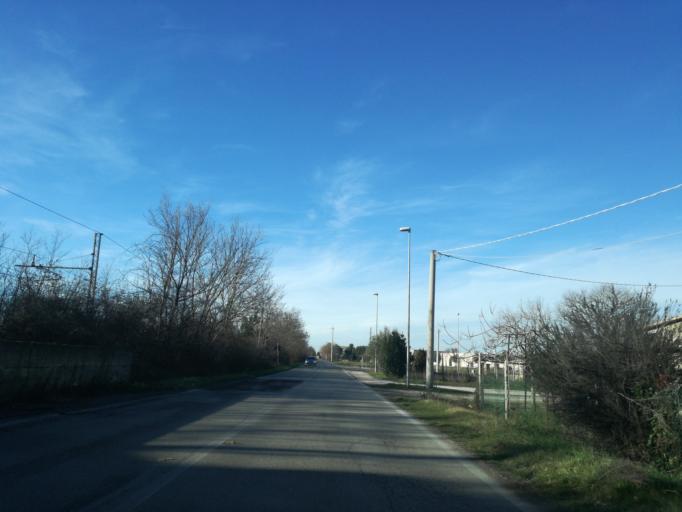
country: IT
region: Umbria
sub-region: Provincia di Perugia
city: Santa Maria degli Angeli
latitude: 43.0498
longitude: 12.5956
